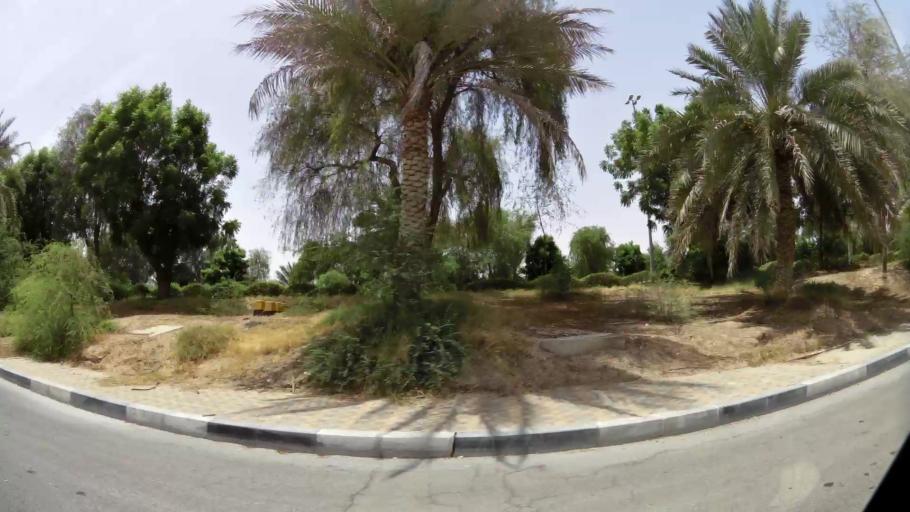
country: AE
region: Abu Dhabi
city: Al Ain
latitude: 24.2053
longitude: 55.7057
